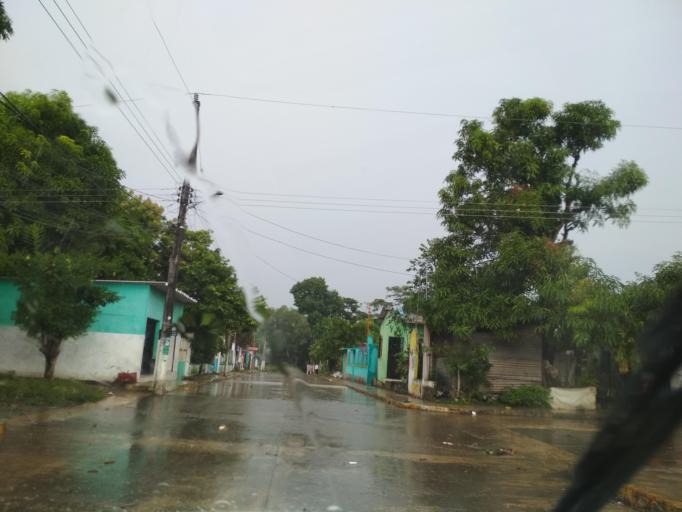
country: MX
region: Veracruz
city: Santiago Tuxtla
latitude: 18.4276
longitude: -95.3209
